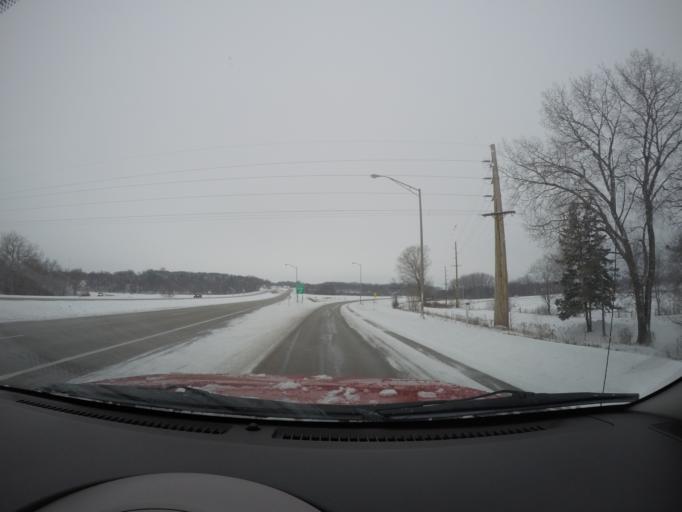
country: US
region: Minnesota
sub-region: Olmsted County
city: Eyota
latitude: 43.9524
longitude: -92.3536
